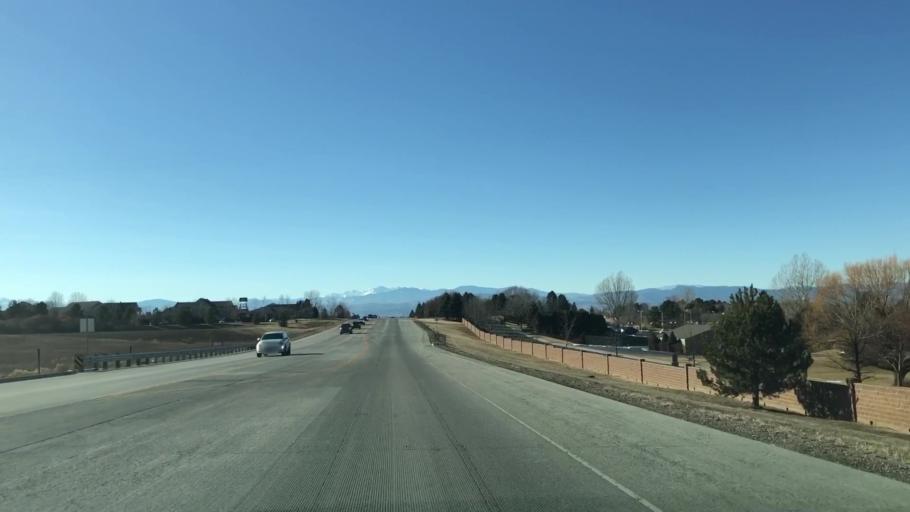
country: US
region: Colorado
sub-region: Weld County
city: Windsor
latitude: 40.4794
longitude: -104.9702
